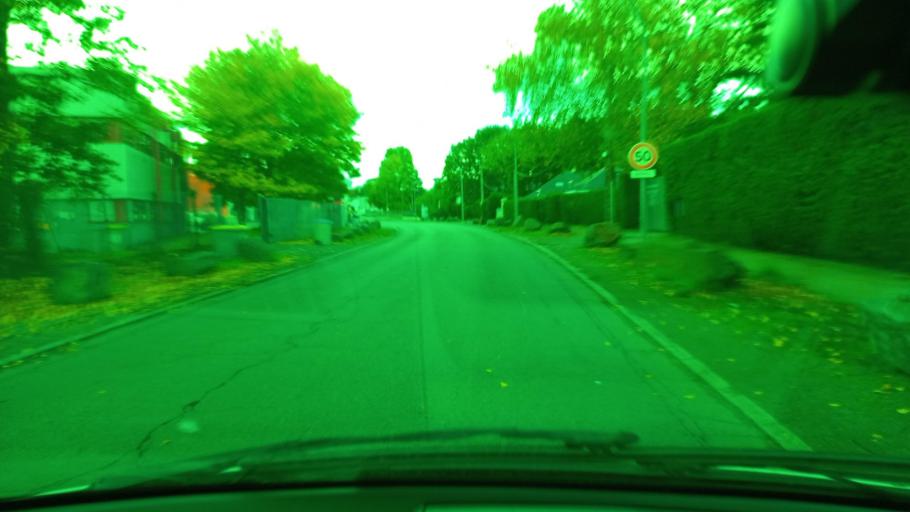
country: FR
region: Pays de la Loire
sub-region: Departement de la Loire-Atlantique
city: Sainte-Luce-sur-Loire
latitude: 47.2489
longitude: -1.4959
